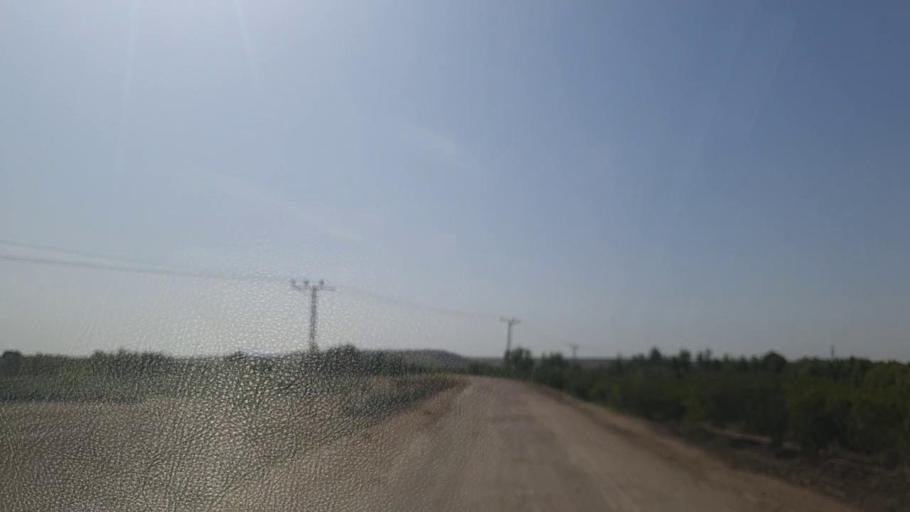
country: PK
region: Sindh
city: Thatta
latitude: 24.6405
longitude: 67.8812
